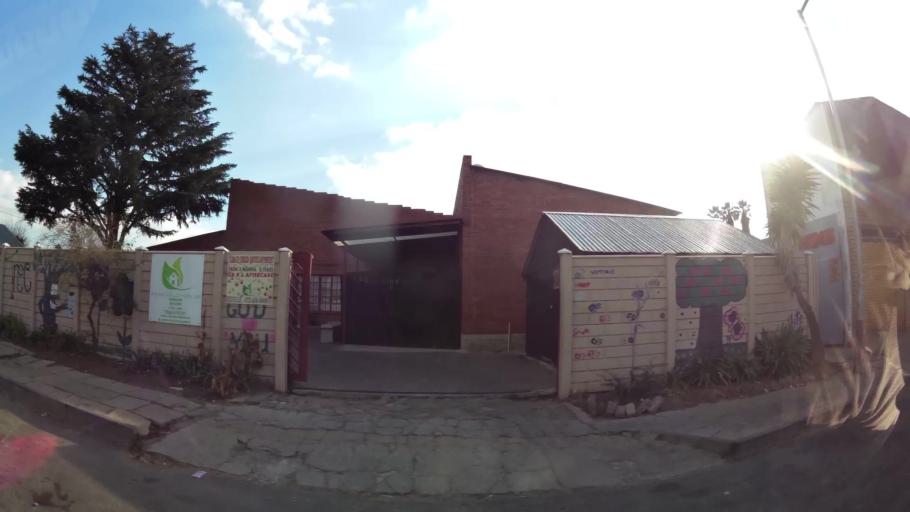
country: ZA
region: Gauteng
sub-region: West Rand District Municipality
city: Krugersdorp
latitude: -26.0986
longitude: 27.7529
